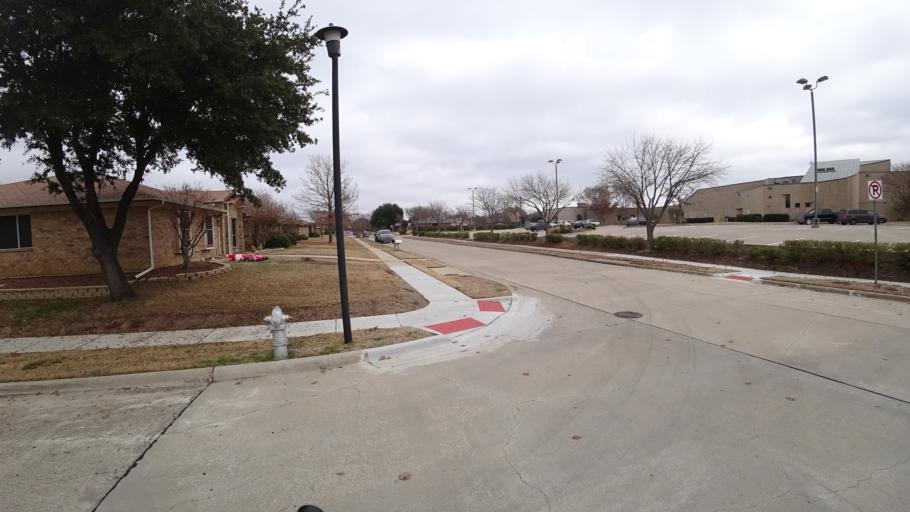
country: US
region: Texas
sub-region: Denton County
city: Highland Village
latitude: 33.0439
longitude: -97.0440
